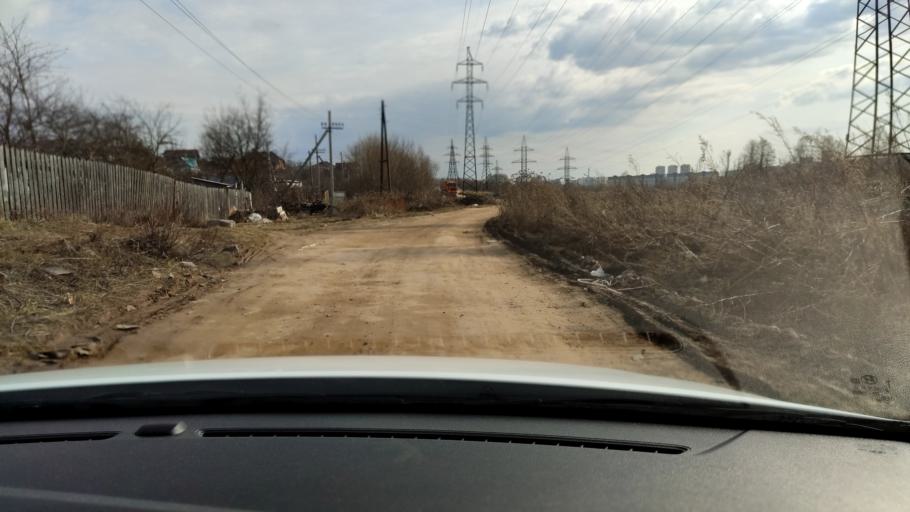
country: RU
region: Tatarstan
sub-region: Gorod Kazan'
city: Kazan
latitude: 55.8188
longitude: 49.2108
